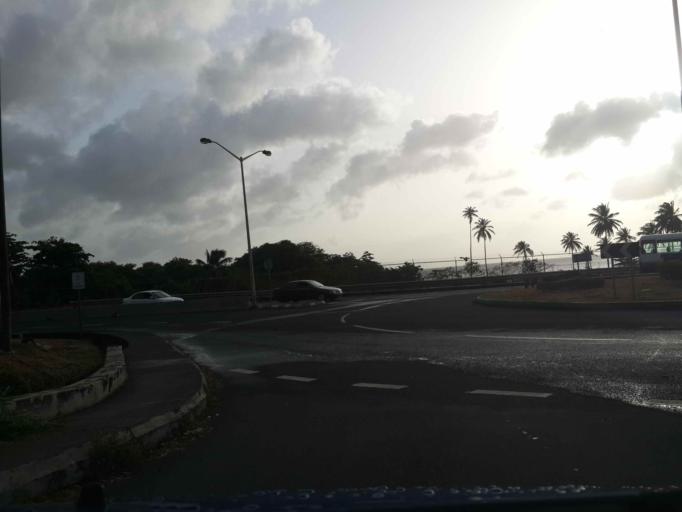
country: LC
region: Castries Quarter
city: Bisee
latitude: 14.0289
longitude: -60.9782
